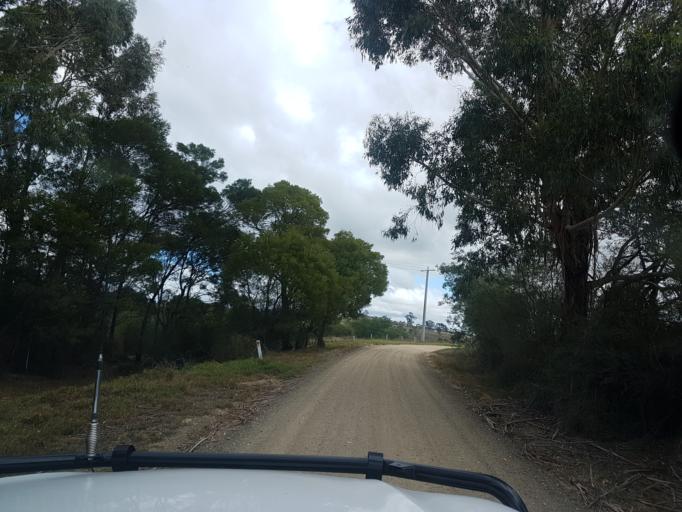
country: AU
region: Victoria
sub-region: East Gippsland
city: Bairnsdale
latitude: -37.7854
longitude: 147.5480
